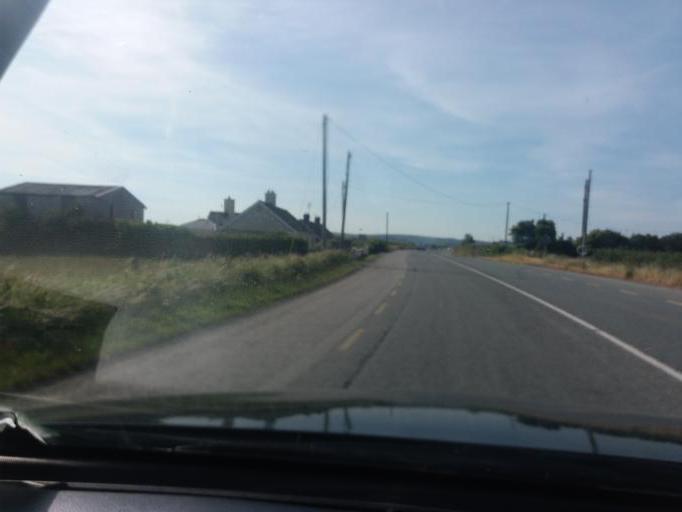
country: IE
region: Leinster
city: Lusk
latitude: 53.5281
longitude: -6.1895
